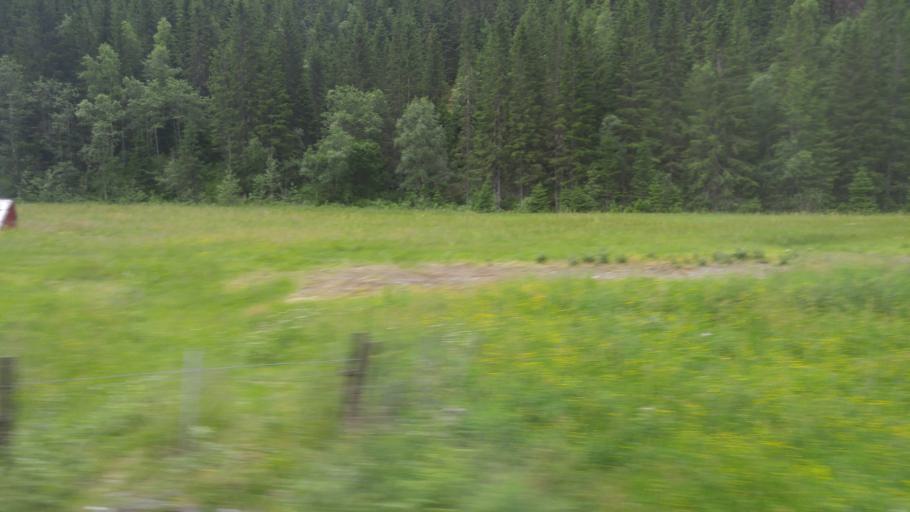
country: NO
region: Nord-Trondelag
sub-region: Meraker
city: Meraker
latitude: 63.4661
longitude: 11.4874
